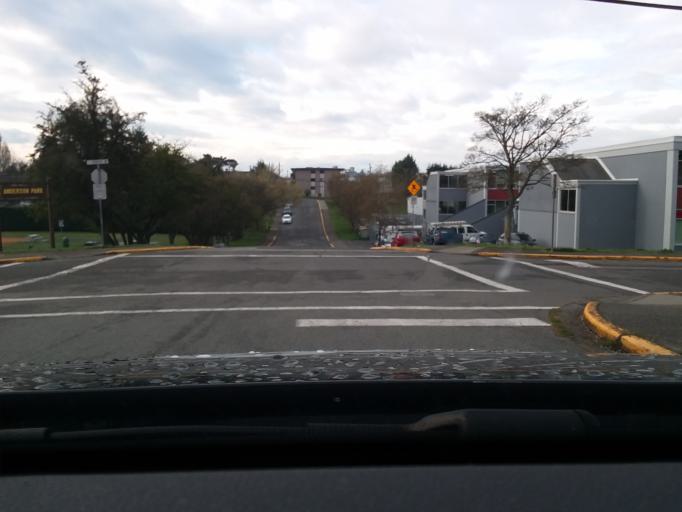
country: CA
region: British Columbia
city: Victoria
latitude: 48.4390
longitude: -123.3958
